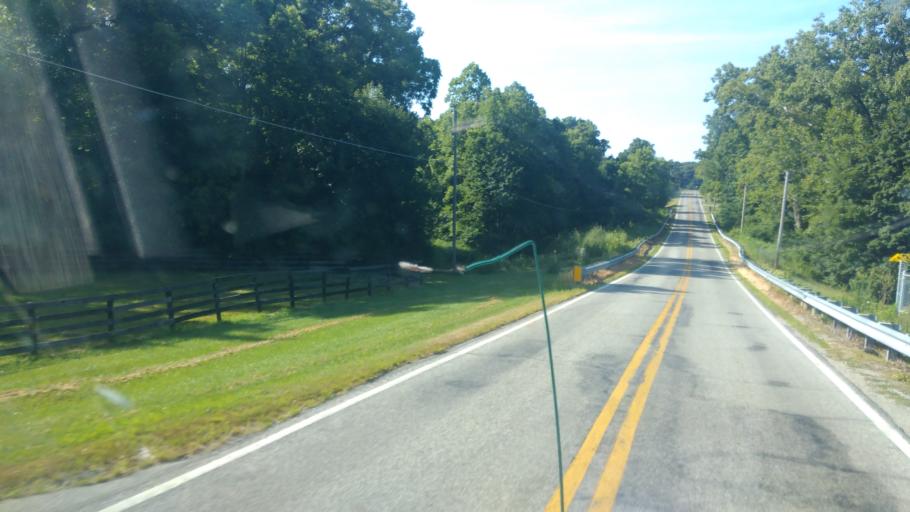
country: US
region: Ohio
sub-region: Delaware County
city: Delaware
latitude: 40.3385
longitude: -83.0517
